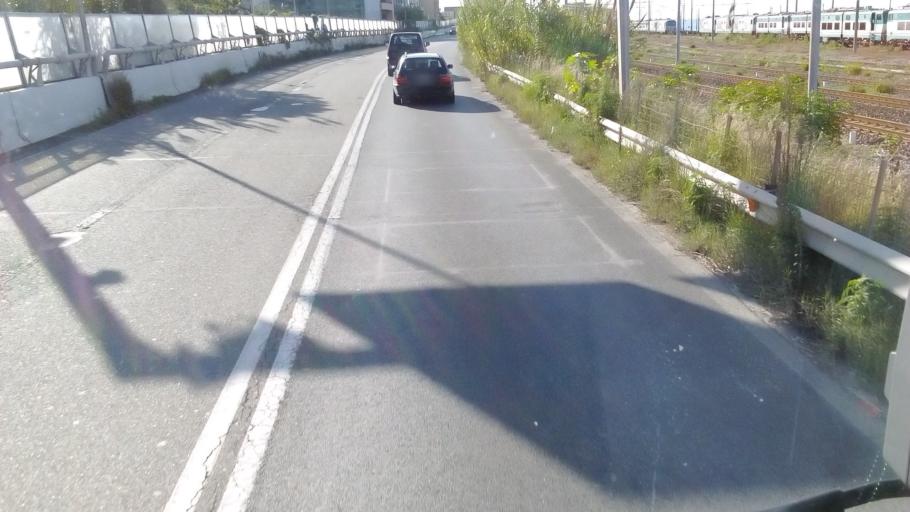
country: IT
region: Calabria
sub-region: Provincia di Reggio Calabria
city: Campo Calabro
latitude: 38.2102
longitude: 15.6355
